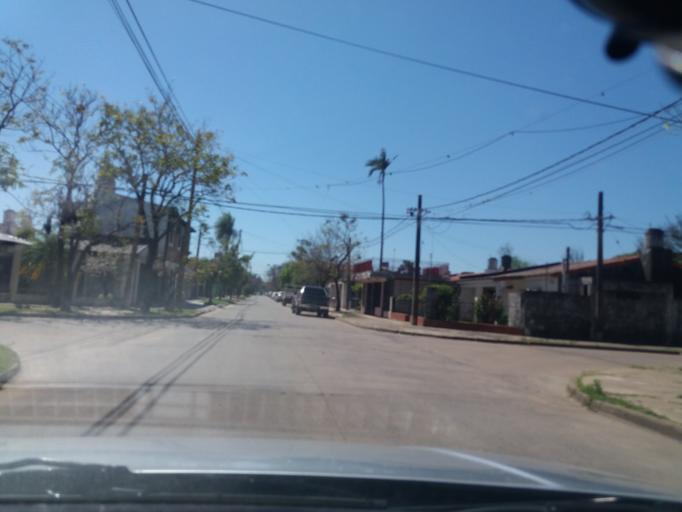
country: AR
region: Corrientes
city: Corrientes
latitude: -27.4875
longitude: -58.8447
